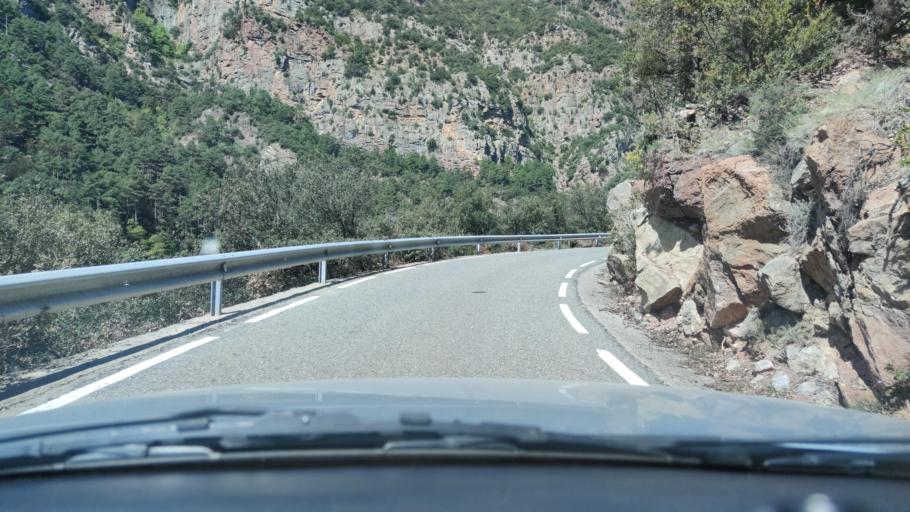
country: ES
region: Catalonia
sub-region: Provincia de Lleida
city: Coll de Nargo
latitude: 42.3004
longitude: 1.2949
